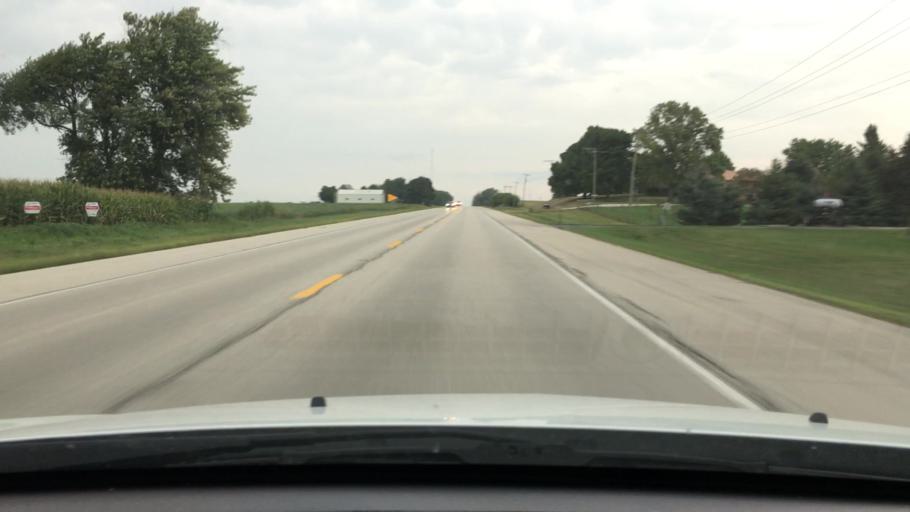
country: US
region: Illinois
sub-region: DeKalb County
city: DeKalb
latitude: 41.8559
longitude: -88.7539
